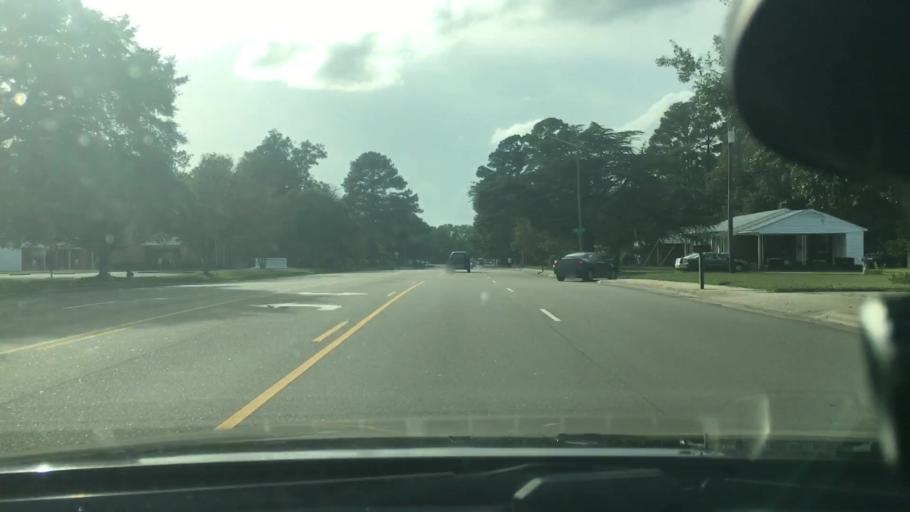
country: US
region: North Carolina
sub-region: Pitt County
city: Summerfield
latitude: 35.5919
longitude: -77.3913
